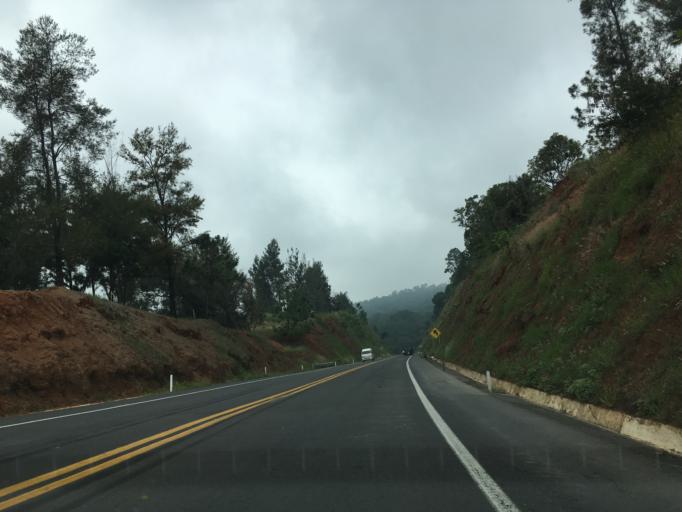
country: MX
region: Michoacan
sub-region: Uruapan
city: Toreo Bajo (El Toreo Bajo)
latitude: 19.4165
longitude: -101.9636
